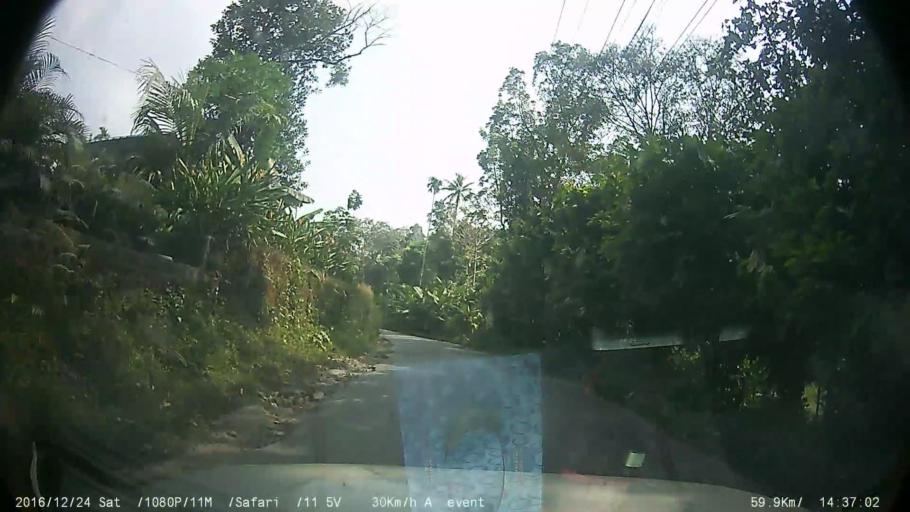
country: IN
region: Kerala
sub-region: Kottayam
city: Lalam
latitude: 9.8029
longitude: 76.7305
